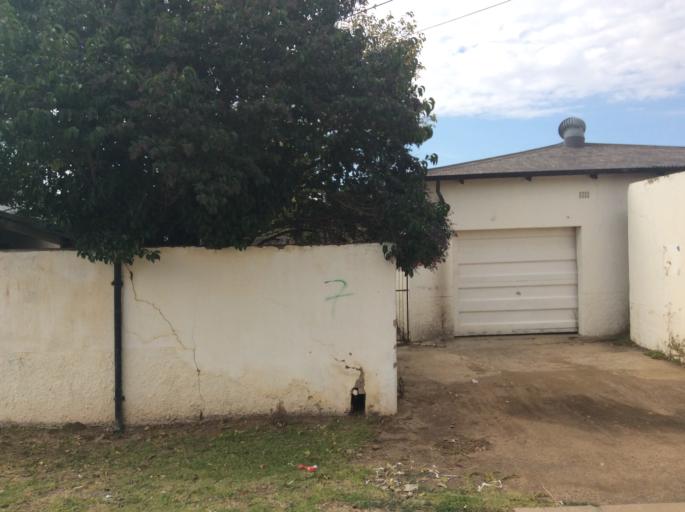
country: LS
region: Mafeteng
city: Mafeteng
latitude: -29.7249
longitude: 27.0390
